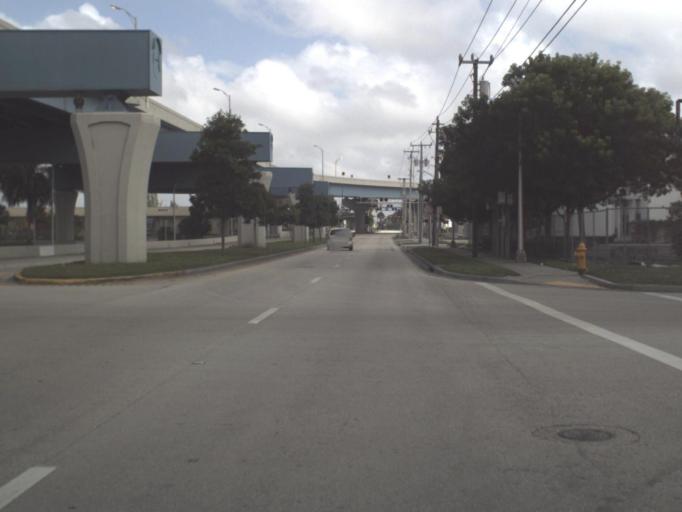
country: US
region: Florida
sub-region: Miami-Dade County
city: Virginia Gardens
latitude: 25.7970
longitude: -80.3109
